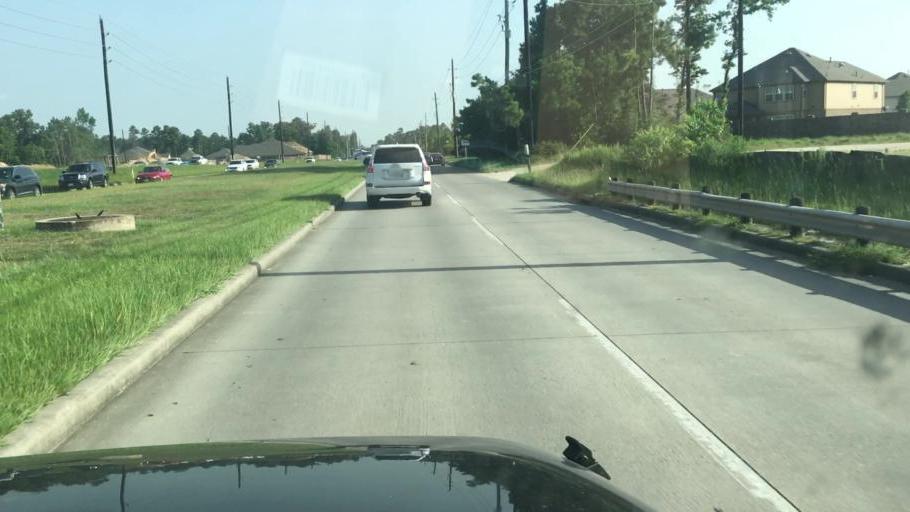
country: US
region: Texas
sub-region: Harris County
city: Atascocita
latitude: 29.9487
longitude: -95.1749
